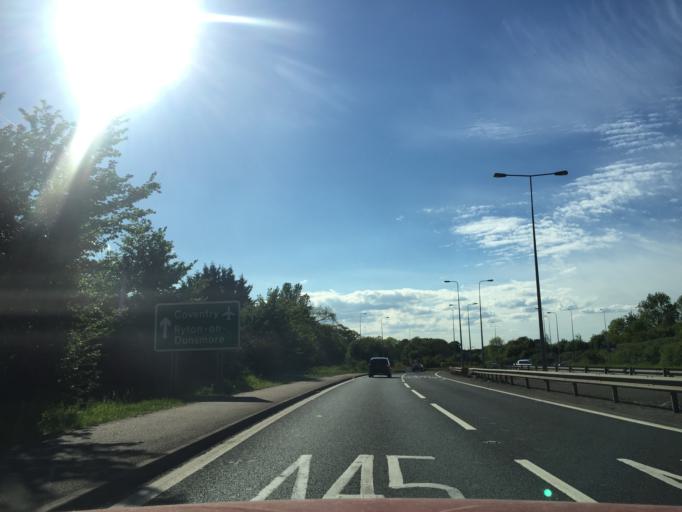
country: GB
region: England
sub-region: Warwickshire
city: Ryton on Dunsmore
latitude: 52.3637
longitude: -1.4240
